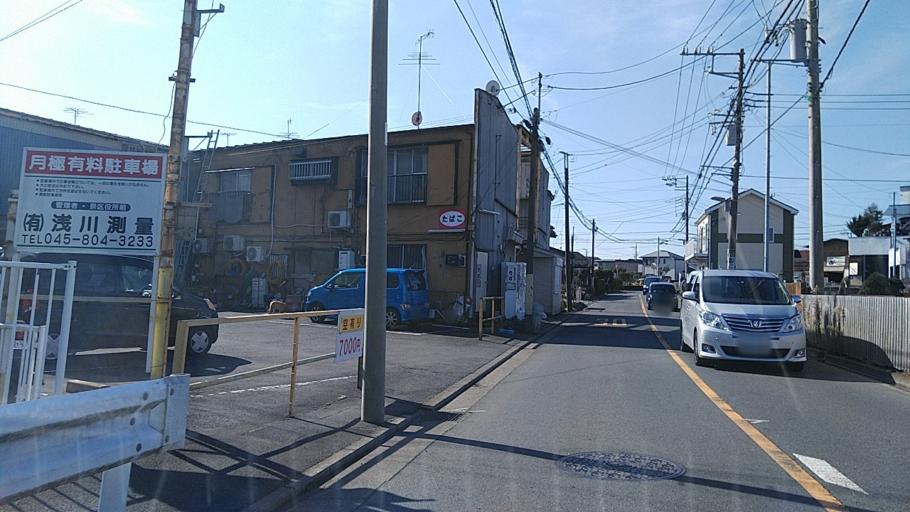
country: JP
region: Kanagawa
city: Fujisawa
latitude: 35.4017
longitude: 139.4926
